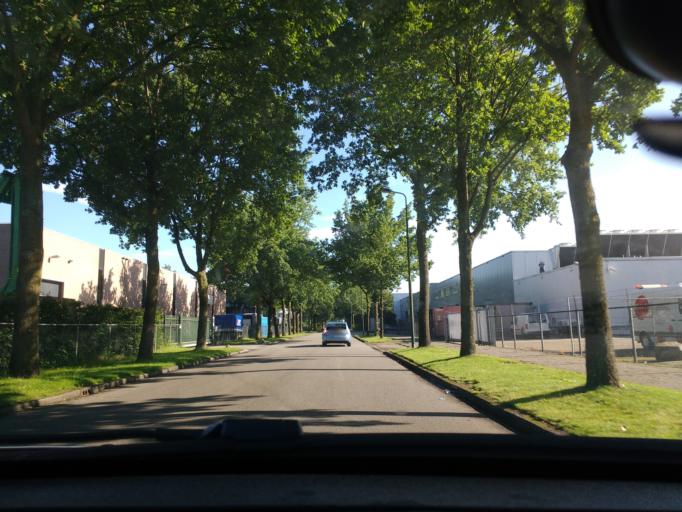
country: NL
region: Utrecht
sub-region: Gemeente Veenendaal
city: Veenendaal
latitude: 52.0397
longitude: 5.5410
